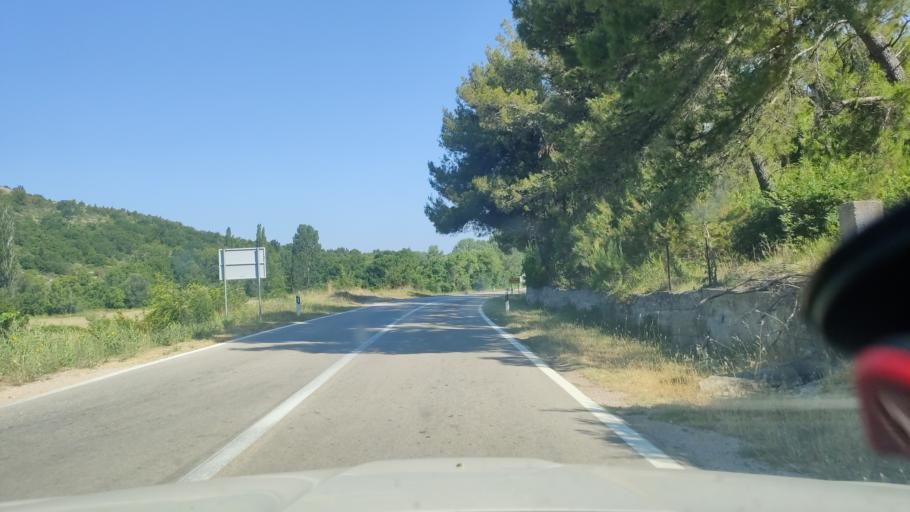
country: HR
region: Sibensko-Kniniska
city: Zaton
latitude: 43.9258
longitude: 15.8153
